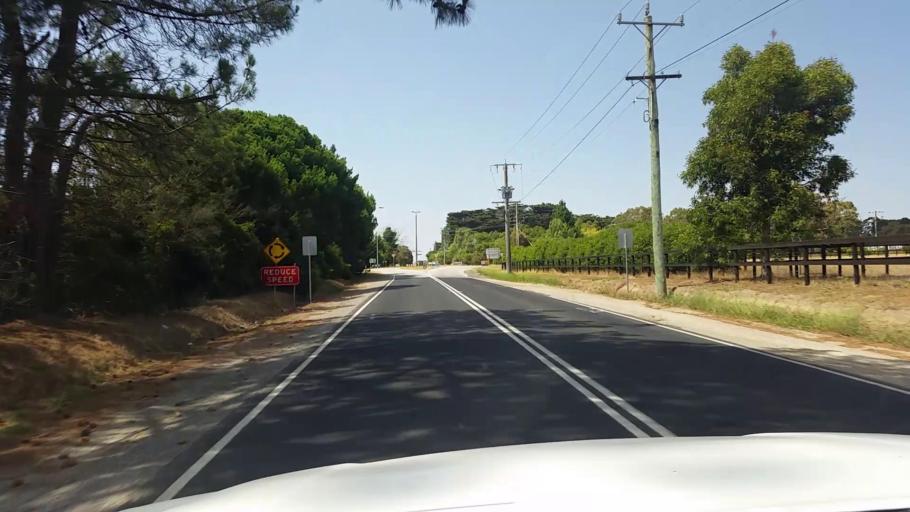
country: AU
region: Victoria
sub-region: Mornington Peninsula
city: Tyabb
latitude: -38.2582
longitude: 145.1438
